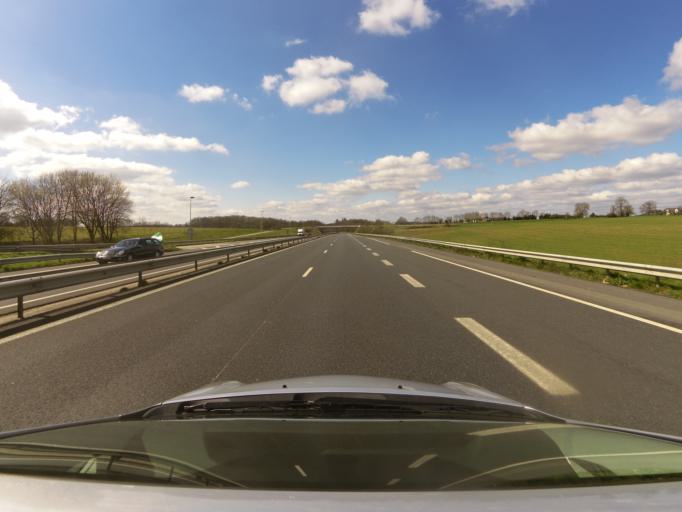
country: FR
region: Haute-Normandie
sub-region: Departement de la Seine-Maritime
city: Saint-Saens
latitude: 49.6761
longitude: 1.3334
